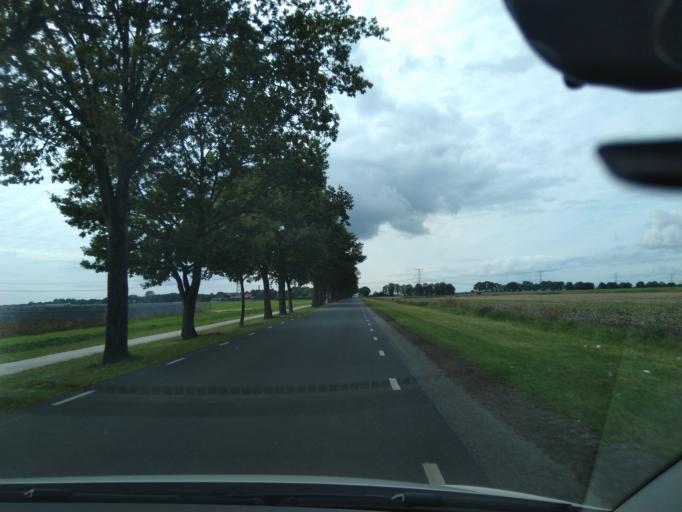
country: NL
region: Groningen
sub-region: Gemeente Pekela
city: Oude Pekela
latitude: 53.0907
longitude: 6.9671
